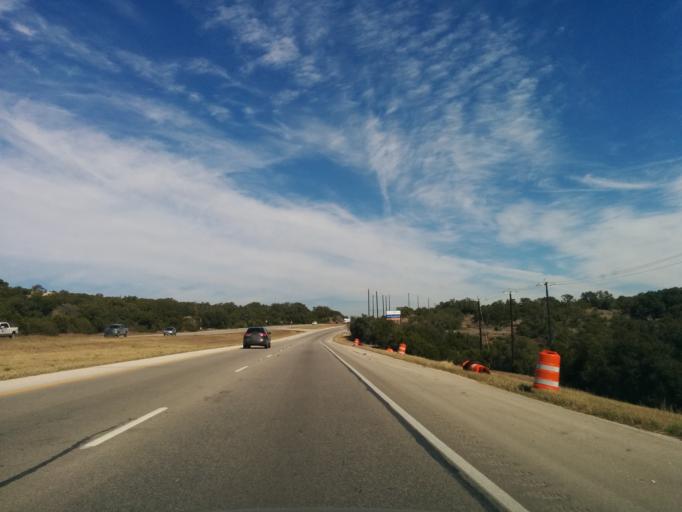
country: US
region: Texas
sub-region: Comal County
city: Bulverde
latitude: 29.7604
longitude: -98.4299
